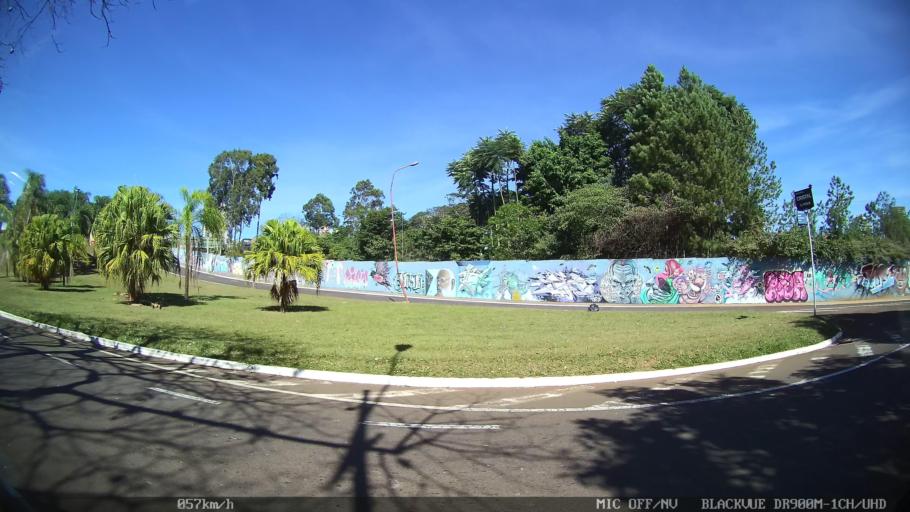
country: BR
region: Sao Paulo
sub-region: Franca
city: Franca
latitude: -20.5525
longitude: -47.4079
